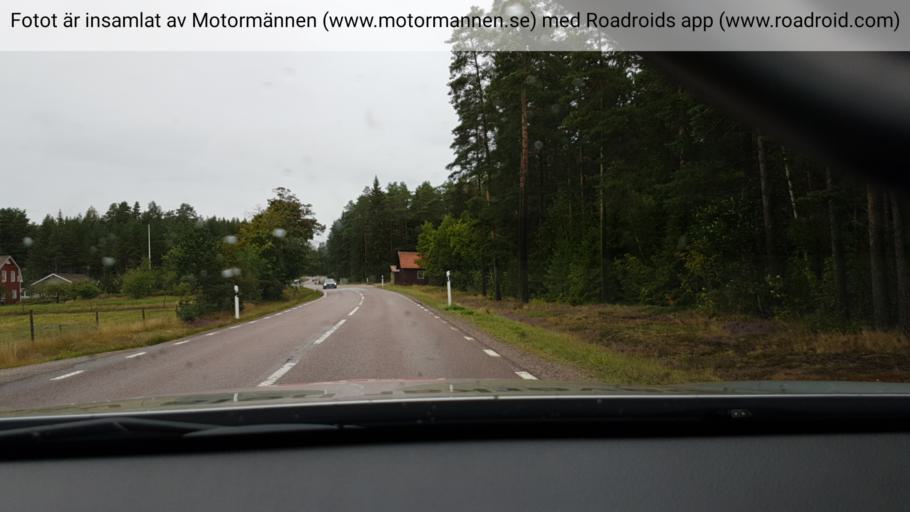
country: SE
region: Gaevleborg
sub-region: Gavle Kommun
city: Hedesunda
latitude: 60.4374
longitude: 16.9665
